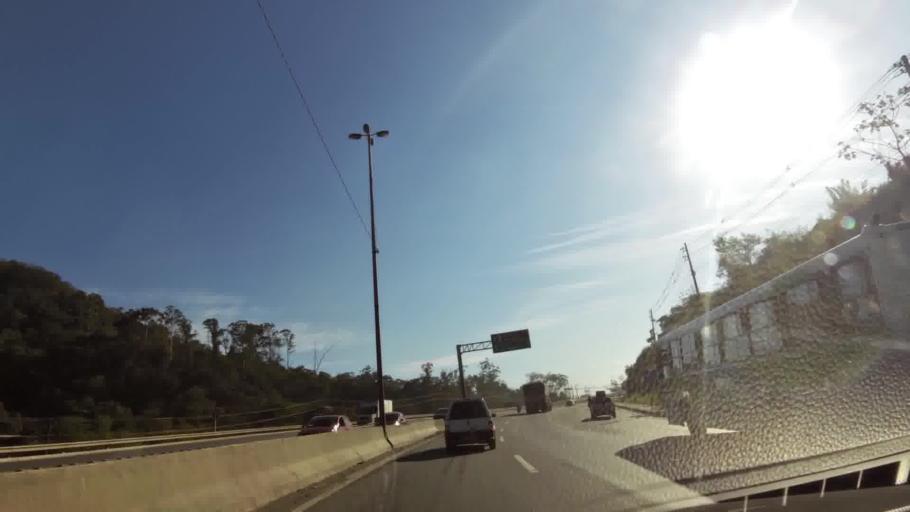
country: BR
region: Espirito Santo
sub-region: Vitoria
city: Vitoria
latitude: -20.3457
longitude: -40.4106
